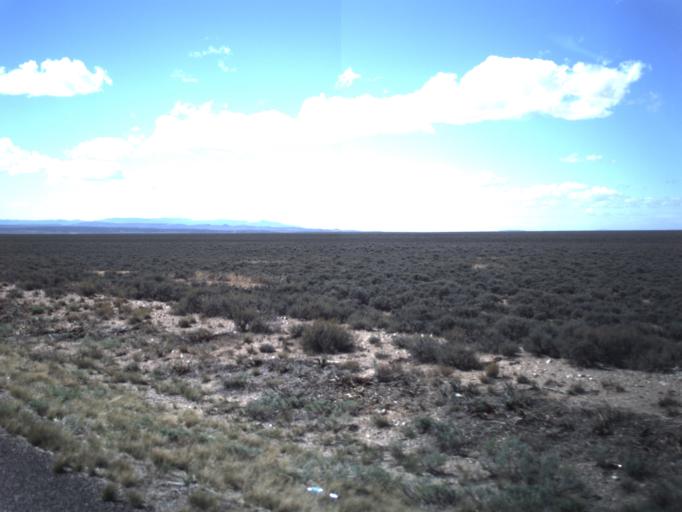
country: US
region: Utah
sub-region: Iron County
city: Enoch
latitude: 37.9441
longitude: -113.0198
